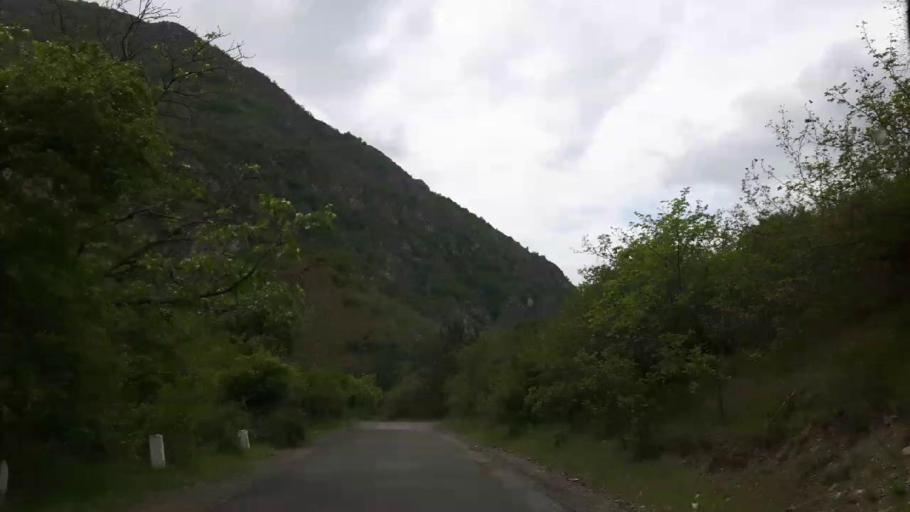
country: GE
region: Shida Kartli
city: Gori
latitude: 41.9003
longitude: 44.0755
